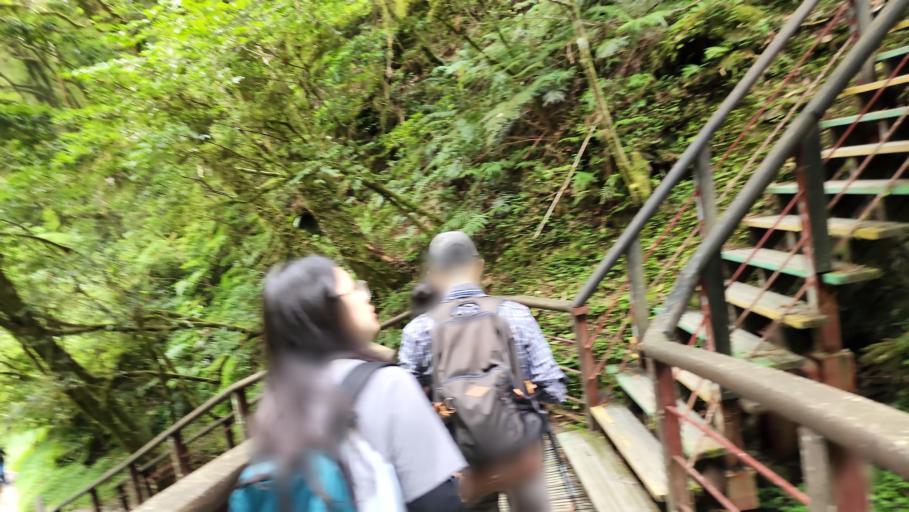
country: TW
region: Taiwan
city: Daxi
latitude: 24.7095
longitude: 121.4408
